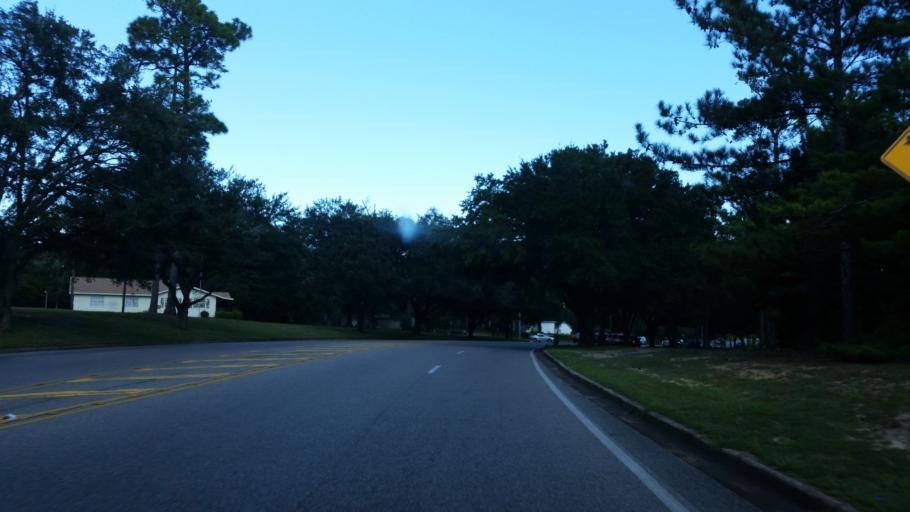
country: US
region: Alabama
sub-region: Mobile County
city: Prichard
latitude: 30.7086
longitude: -88.1537
